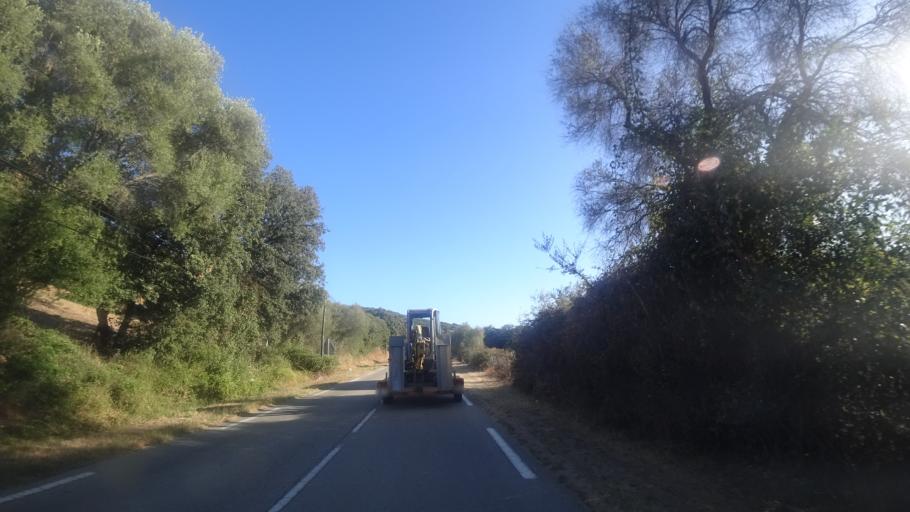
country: FR
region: Corsica
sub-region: Departement de la Corse-du-Sud
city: Cargese
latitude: 42.1535
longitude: 8.6066
